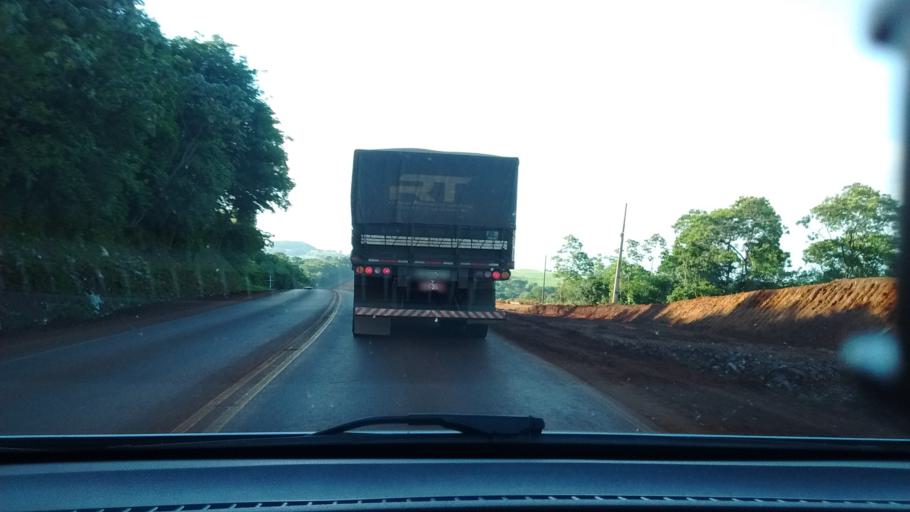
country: BR
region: Parana
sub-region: Cascavel
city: Cascavel
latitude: -25.2088
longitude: -53.5977
